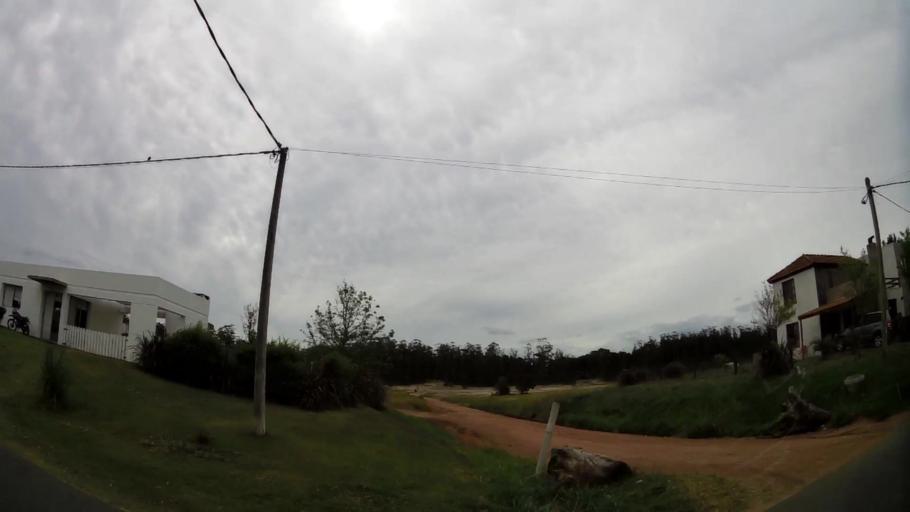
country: UY
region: Maldonado
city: Maldonado
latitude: -34.9052
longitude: -54.9743
